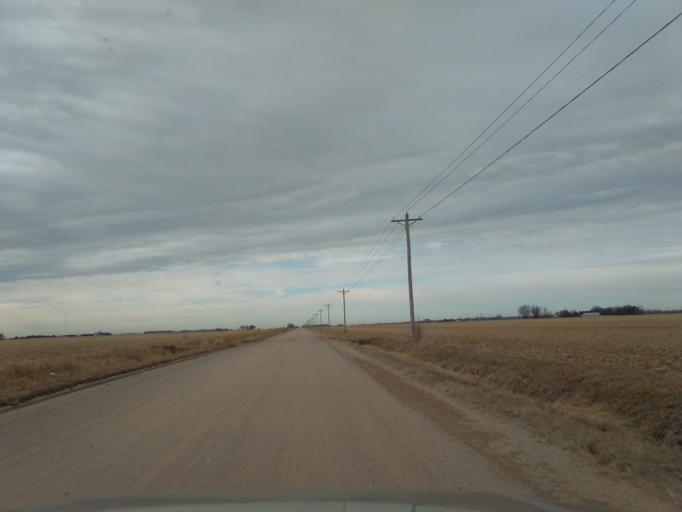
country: US
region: Nebraska
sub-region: Buffalo County
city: Gibbon
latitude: 40.6408
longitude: -98.9037
